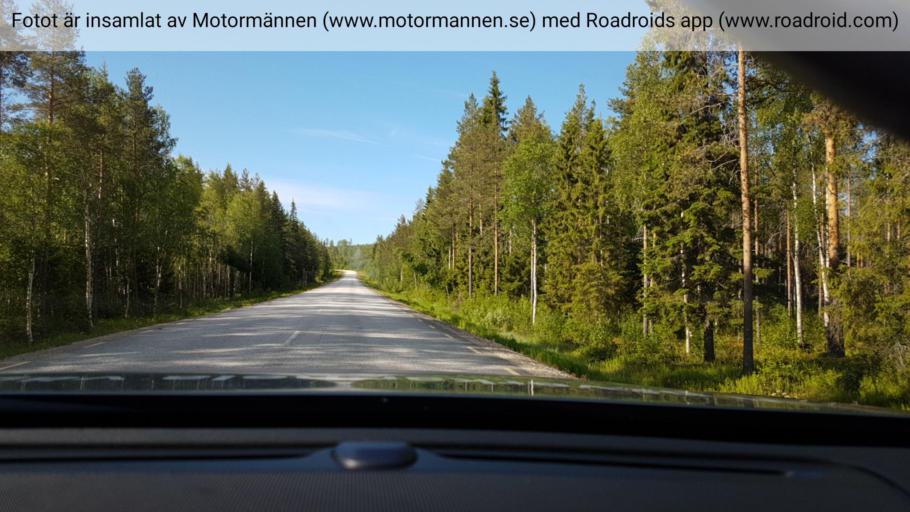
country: SE
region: Vaesterbotten
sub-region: Vindelns Kommun
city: Vindeln
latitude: 64.1906
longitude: 19.4076
